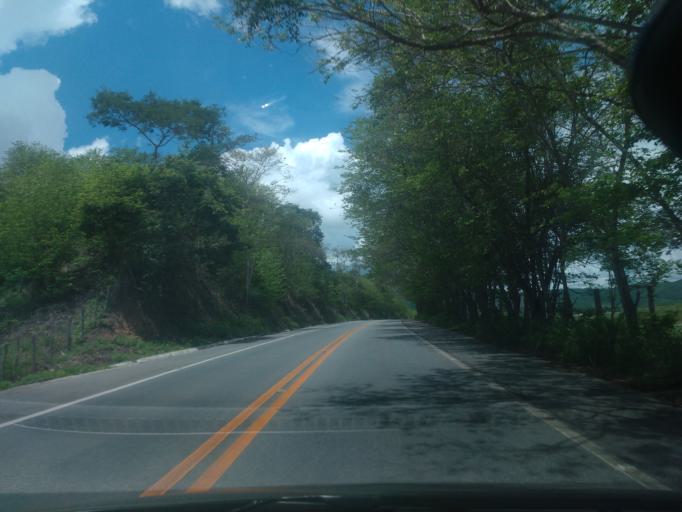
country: BR
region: Alagoas
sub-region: Uniao Dos Palmares
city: Uniao dos Palmares
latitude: -9.1389
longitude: -36.0183
